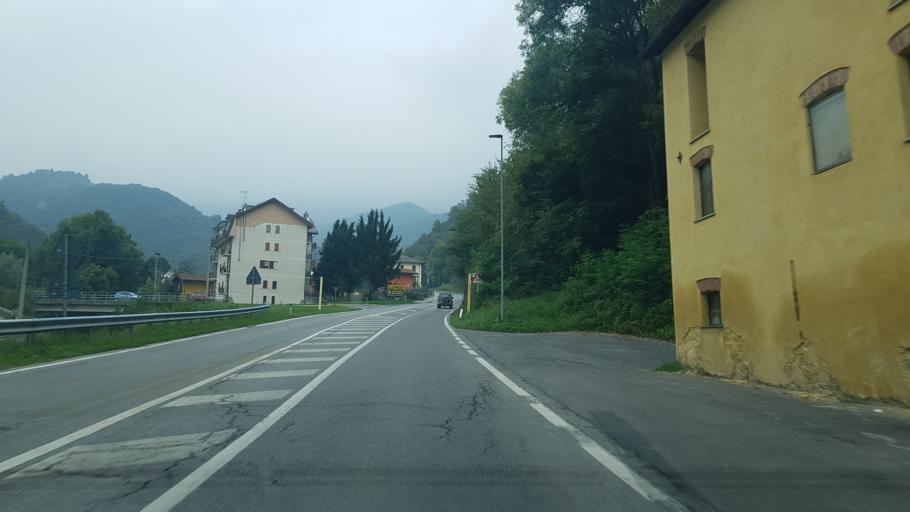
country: IT
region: Piedmont
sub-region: Provincia di Cuneo
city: Frabosa Sottana
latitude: 44.3079
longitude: 7.8020
